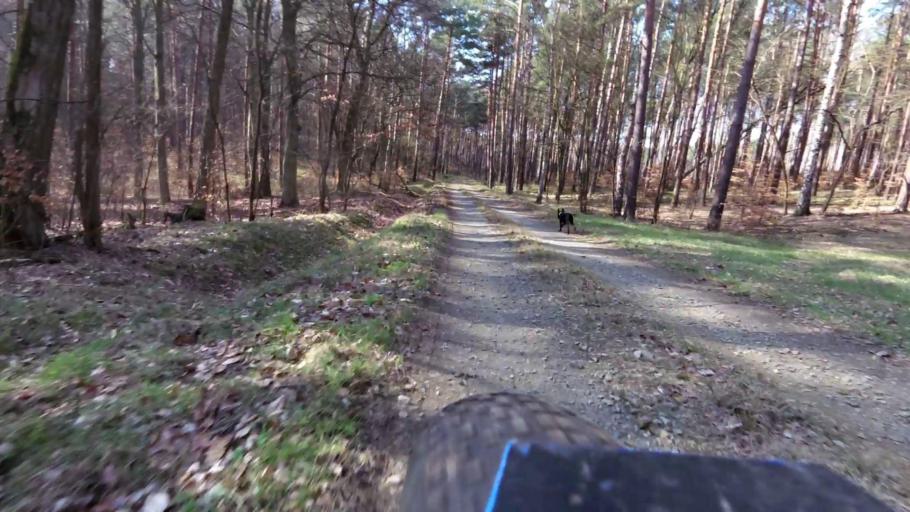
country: PL
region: Lubusz
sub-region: Powiat slubicki
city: Cybinka
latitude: 52.2317
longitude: 14.8273
